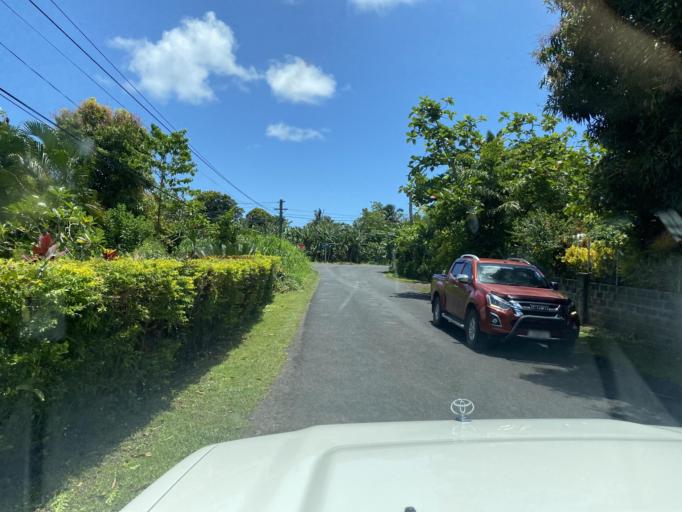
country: WS
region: Tuamasaga
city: Apia
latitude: -13.8377
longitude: -171.7572
